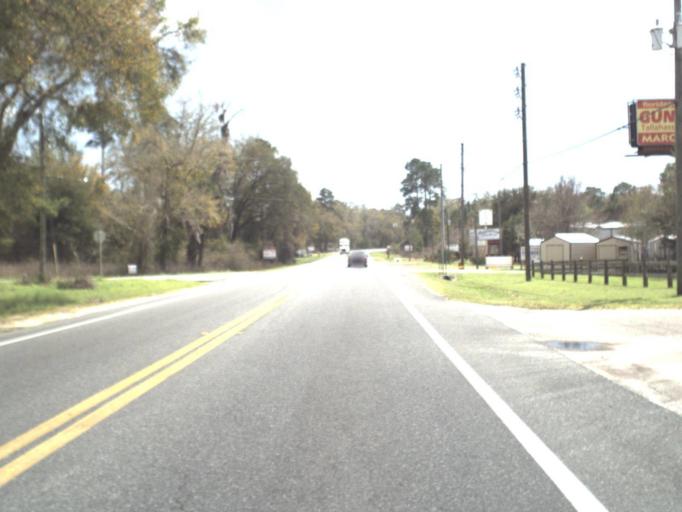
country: US
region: Florida
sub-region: Wakulla County
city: Crawfordville
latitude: 30.1242
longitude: -84.3858
